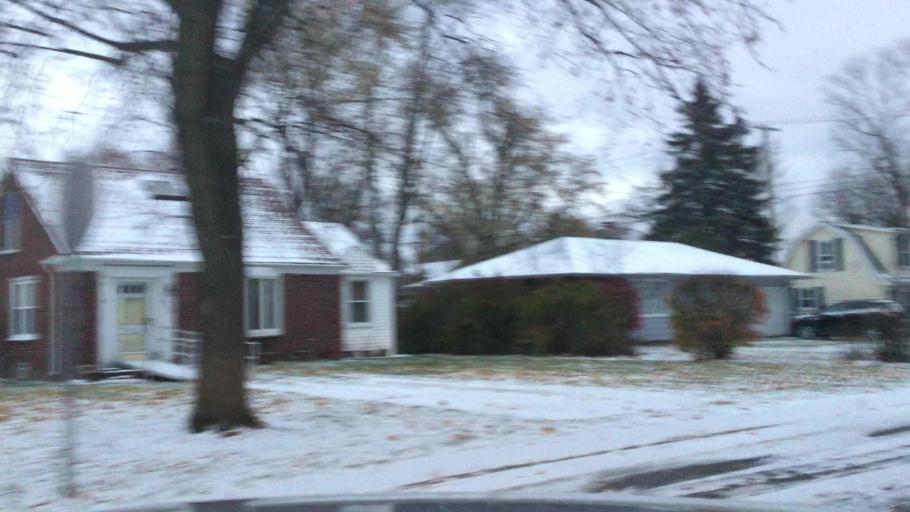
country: US
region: Michigan
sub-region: Livingston County
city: Brighton
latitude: 42.5302
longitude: -83.7912
